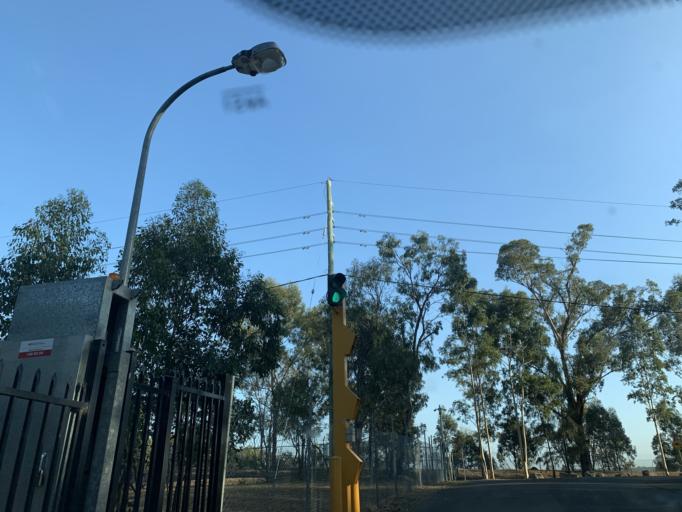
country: AU
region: New South Wales
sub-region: Fairfield
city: Horsley Park
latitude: -33.8352
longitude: 150.8826
